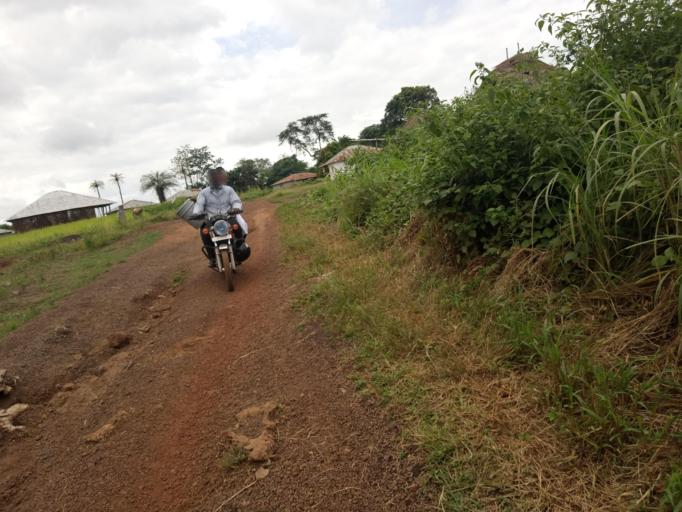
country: SL
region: Northern Province
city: Kamakwie
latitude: 9.4814
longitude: -12.2509
